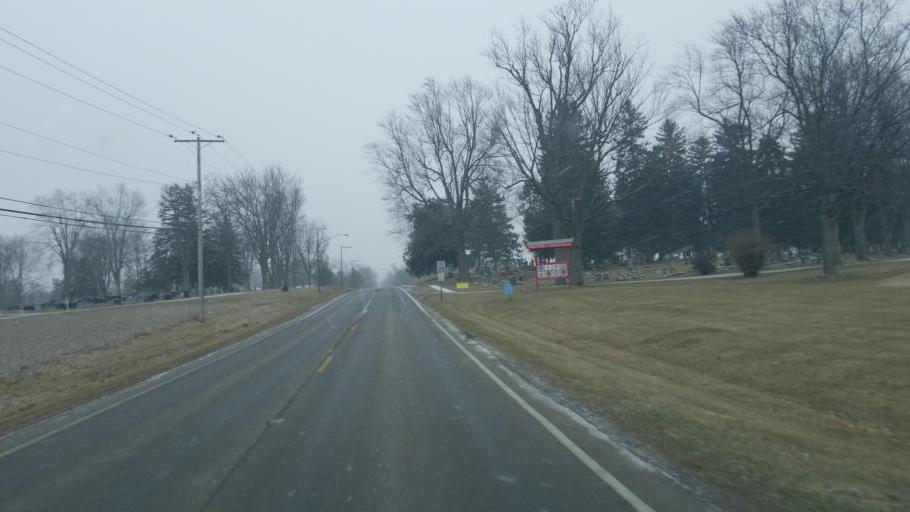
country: US
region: Ohio
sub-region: Defiance County
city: Hicksville
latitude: 41.3037
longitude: -84.7773
